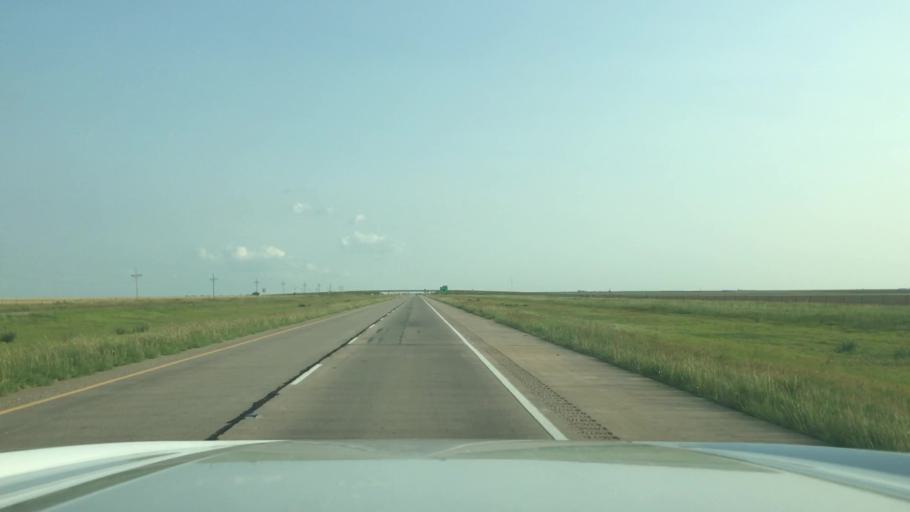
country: US
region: Texas
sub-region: Randall County
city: Canyon
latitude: 34.8950
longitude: -101.8488
